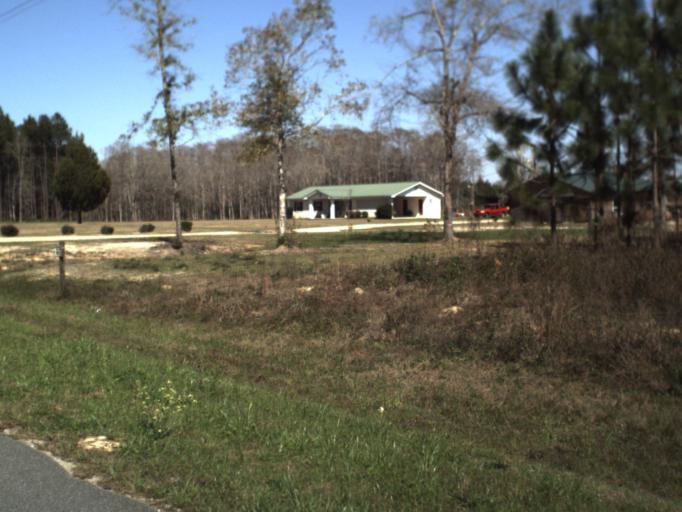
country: US
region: Florida
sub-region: Calhoun County
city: Blountstown
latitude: 30.3073
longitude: -85.1285
